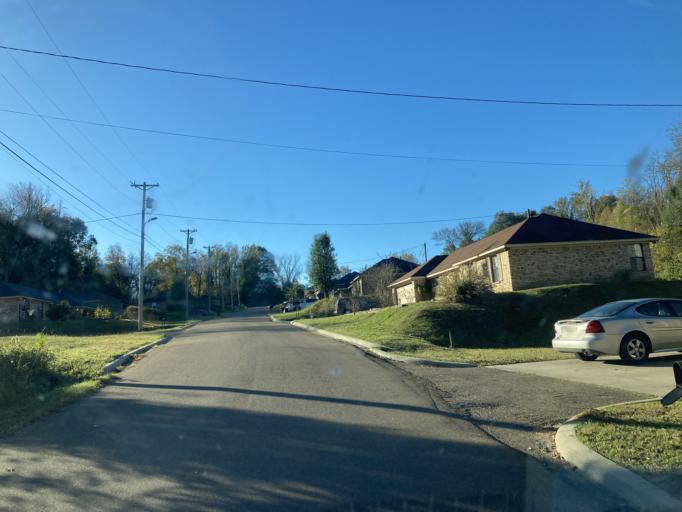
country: US
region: Mississippi
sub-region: Yazoo County
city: Yazoo City
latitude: 32.8496
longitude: -90.4032
